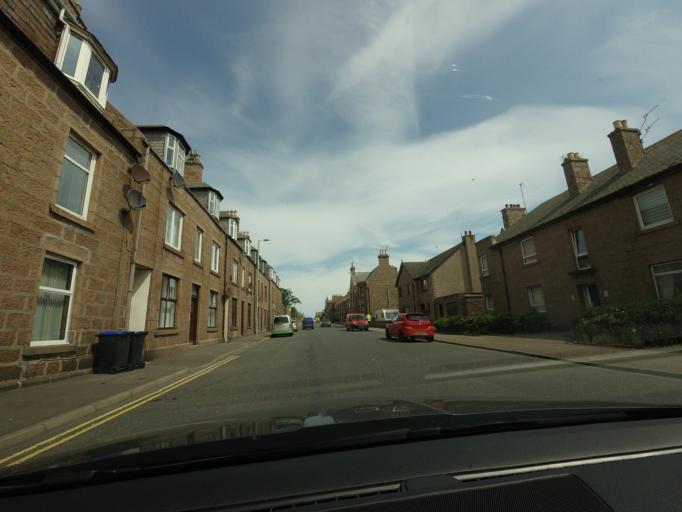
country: GB
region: Scotland
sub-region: Aberdeenshire
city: Peterhead
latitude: 57.5060
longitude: -1.7873
